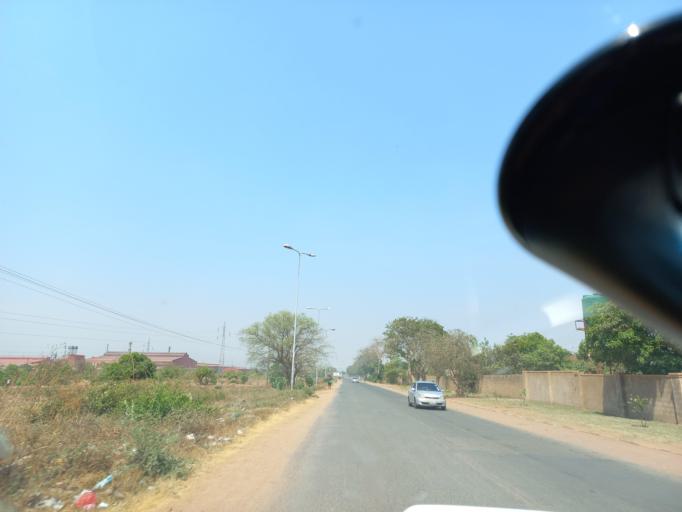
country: ZM
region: Lusaka
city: Kafue
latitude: -15.7414
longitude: 28.1721
